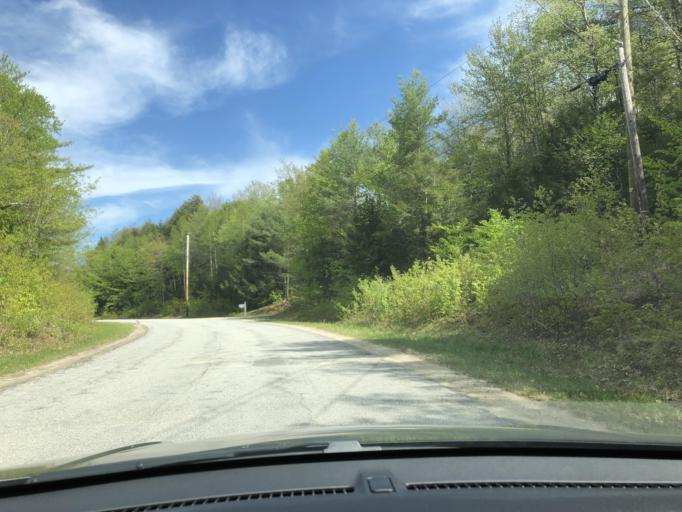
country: US
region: New Hampshire
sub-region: Merrimack County
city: New London
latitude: 43.4093
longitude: -72.0284
